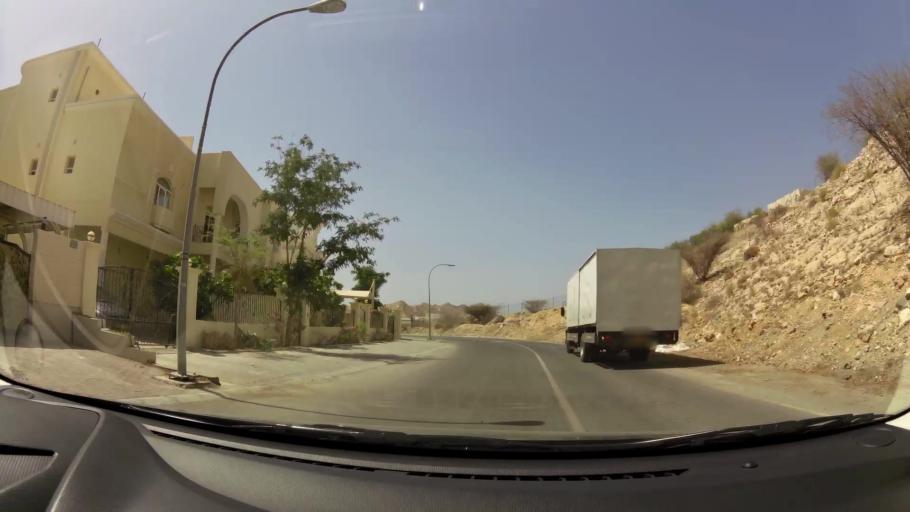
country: OM
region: Muhafazat Masqat
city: Muscat
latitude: 23.6202
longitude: 58.5089
